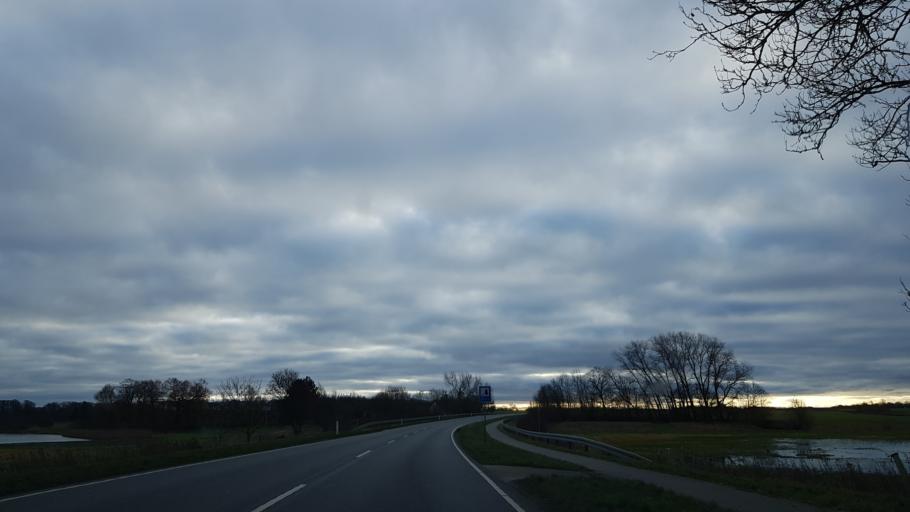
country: DK
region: Zealand
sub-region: Kalundborg Kommune
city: Gorlev
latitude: 55.5667
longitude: 11.1967
